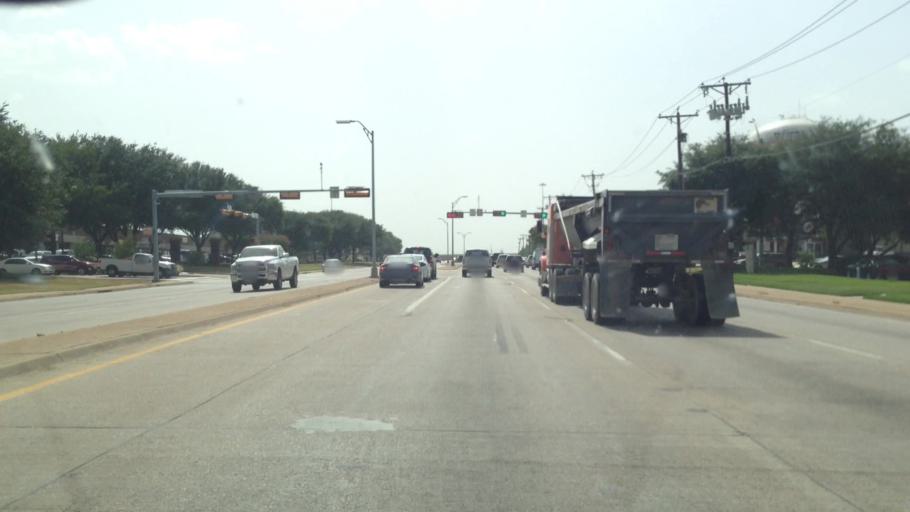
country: US
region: Texas
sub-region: Collin County
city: McKinney
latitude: 33.2165
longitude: -96.6307
